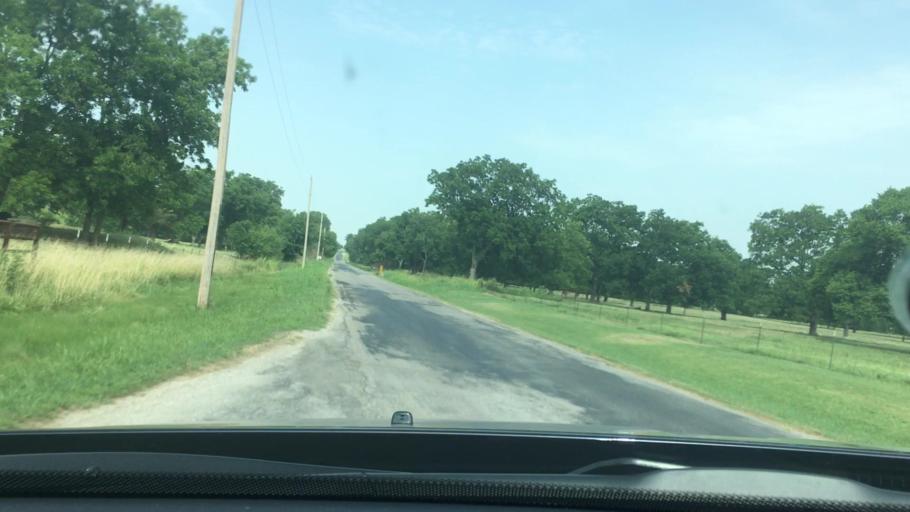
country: US
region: Oklahoma
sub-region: Garvin County
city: Pauls Valley
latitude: 34.8258
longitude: -97.1963
